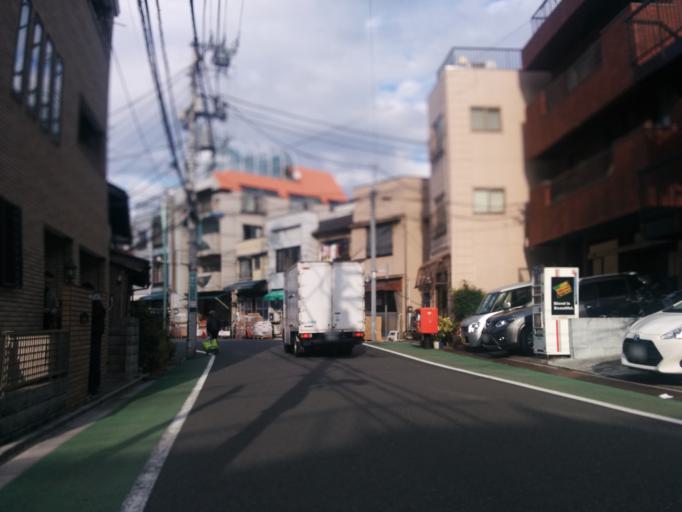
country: JP
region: Tokyo
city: Tokyo
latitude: 35.7157
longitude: 139.7532
